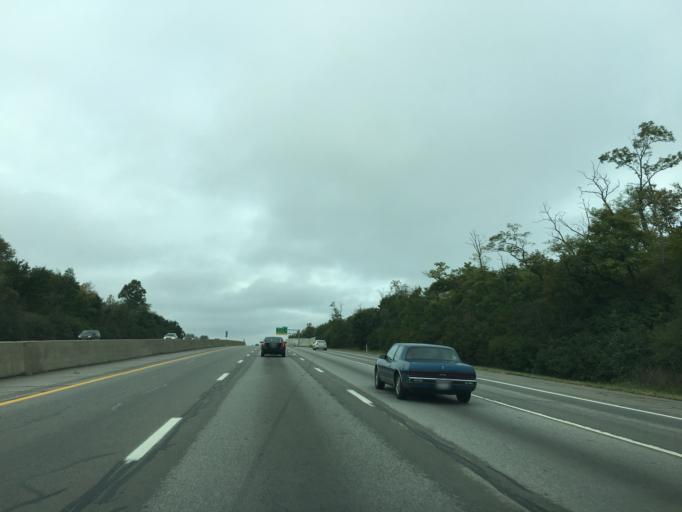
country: US
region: Ohio
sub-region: Hamilton County
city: Forest Park
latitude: 39.2994
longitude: -84.5085
